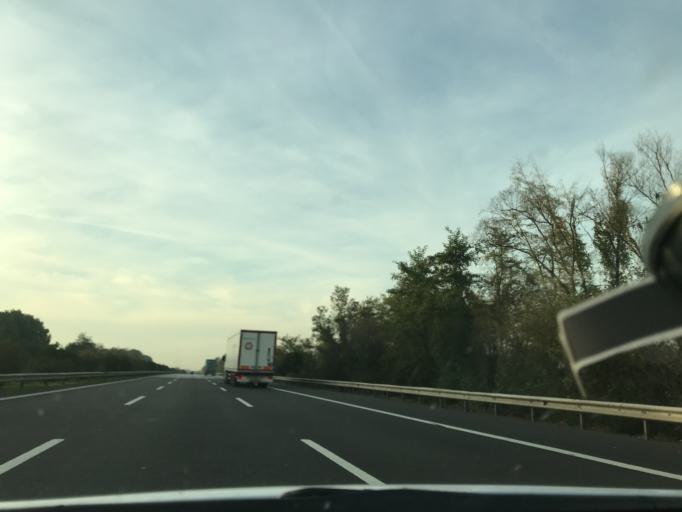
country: TR
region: Duzce
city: Cilimli
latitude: 40.8204
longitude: 31.0712
